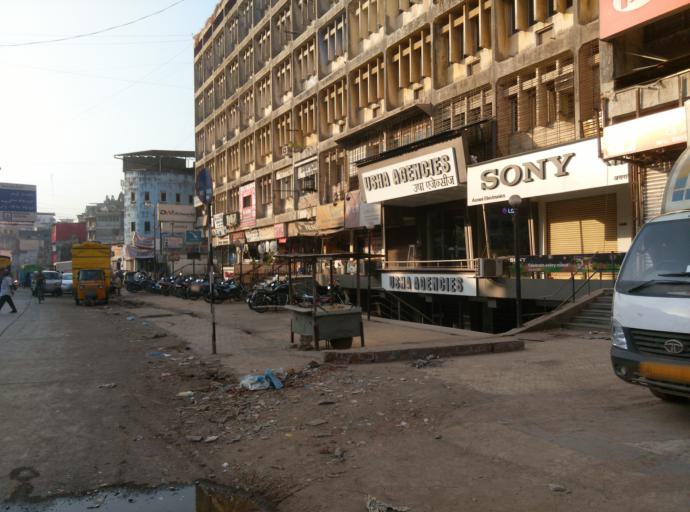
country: IN
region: Maharashtra
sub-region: Thane
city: Ulhasnagar
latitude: 19.2280
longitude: 73.1608
